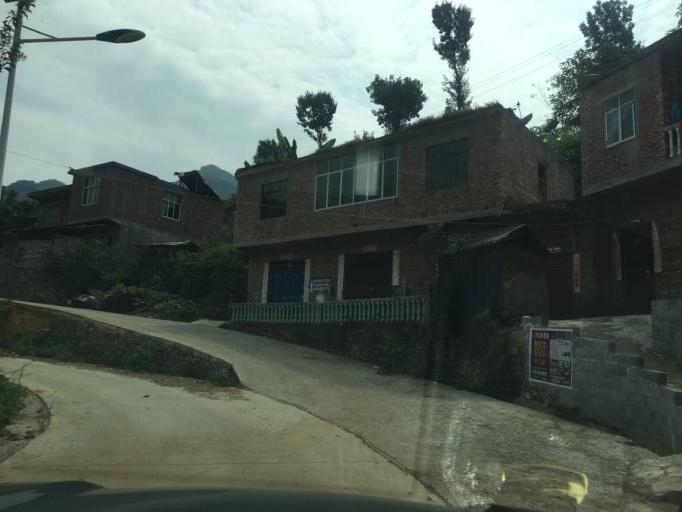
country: CN
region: Guizhou Sheng
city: Anshun
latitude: 25.4330
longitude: 105.9632
